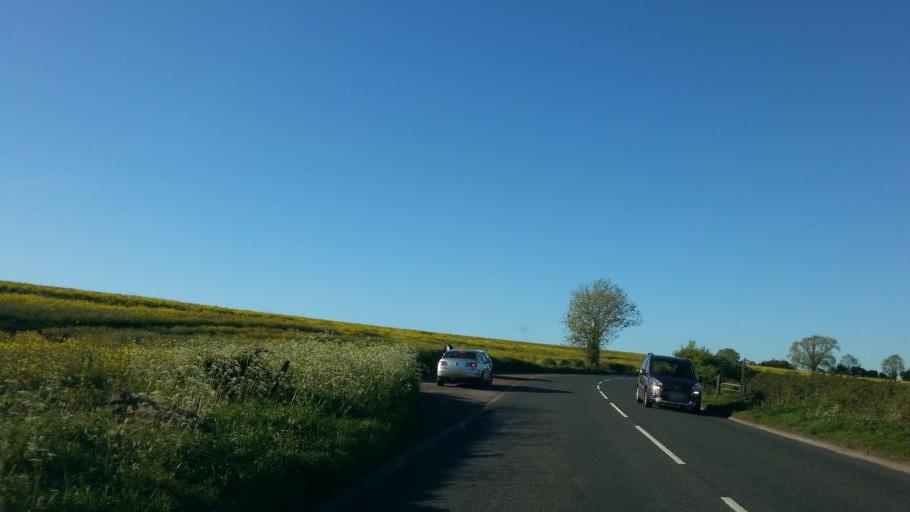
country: GB
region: England
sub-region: Bath and North East Somerset
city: Clutton
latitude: 51.3400
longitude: -2.5478
